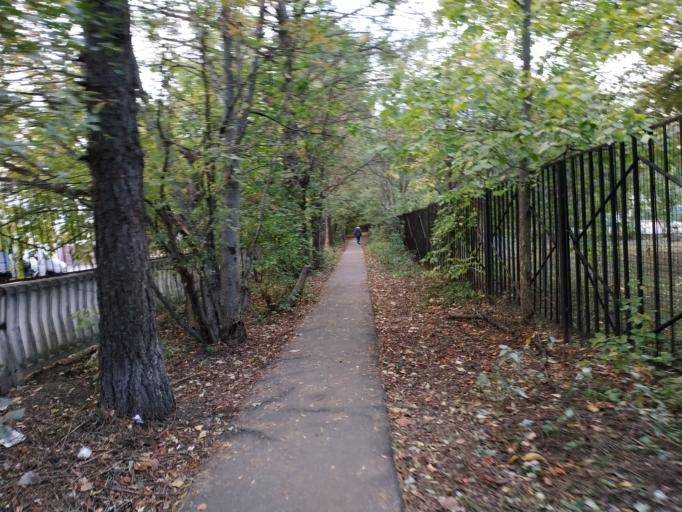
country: RU
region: Moscow
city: Khimki
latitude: 55.8661
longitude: 37.4319
